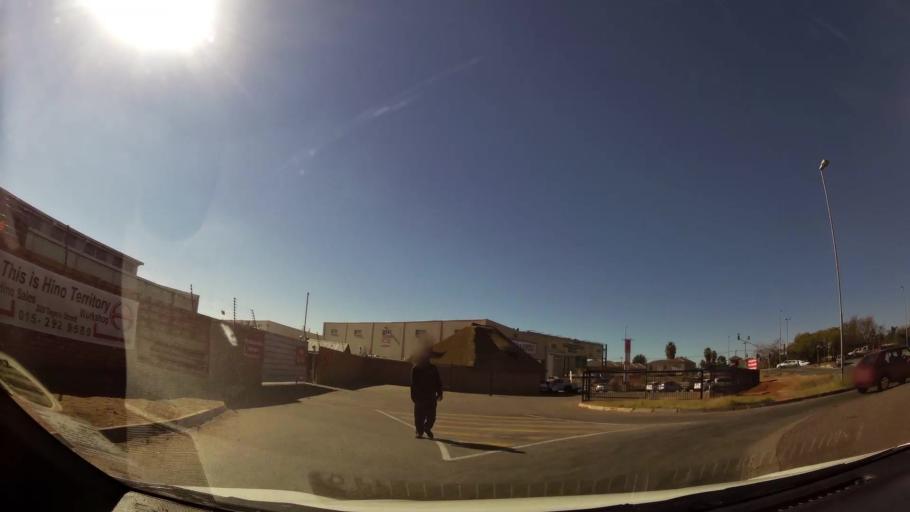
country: ZA
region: Limpopo
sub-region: Capricorn District Municipality
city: Polokwane
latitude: -23.9164
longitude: 29.4416
